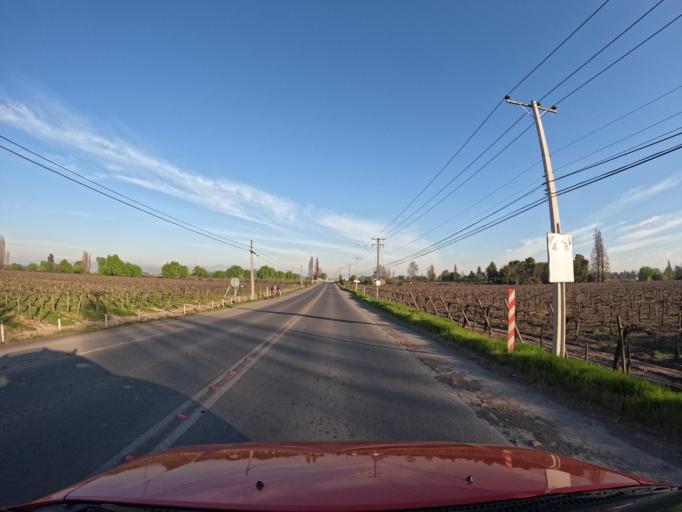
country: CL
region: Maule
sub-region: Provincia de Curico
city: Curico
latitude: -34.9560
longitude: -71.2538
